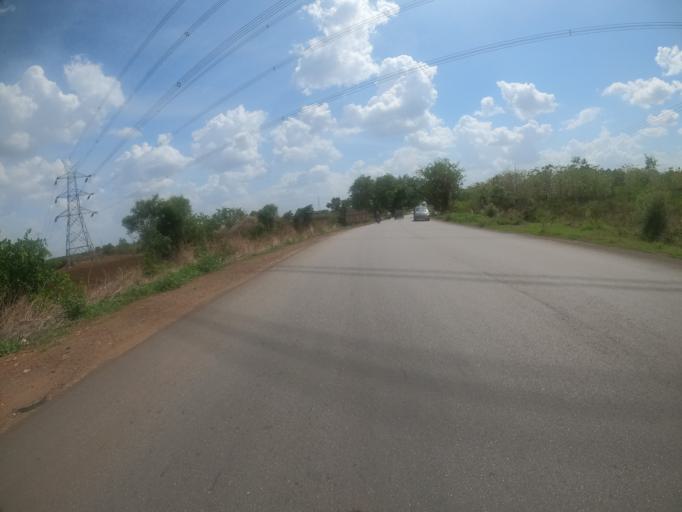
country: IN
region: Telangana
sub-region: Rangareddi
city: Singapur
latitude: 17.3045
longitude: 78.0864
